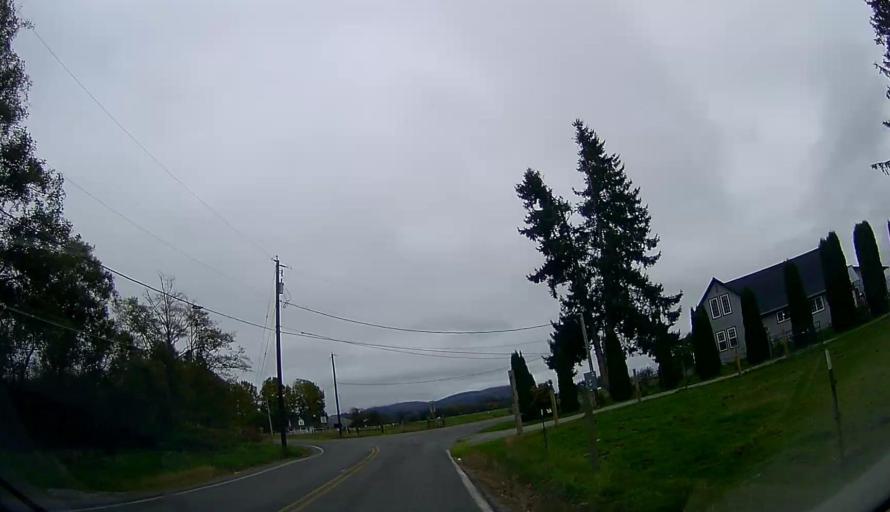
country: US
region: Washington
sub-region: Skagit County
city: Sedro-Woolley
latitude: 48.5151
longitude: -122.1403
